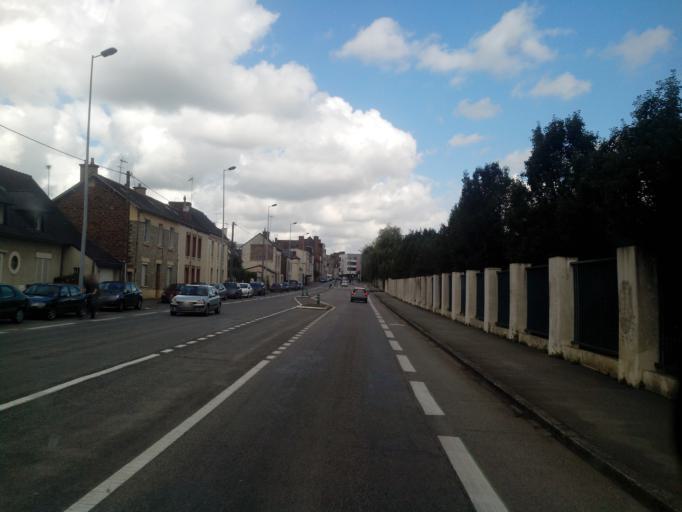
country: FR
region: Brittany
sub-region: Departement d'Ille-et-Vilaine
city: Rennes
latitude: 48.1121
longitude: -1.6561
